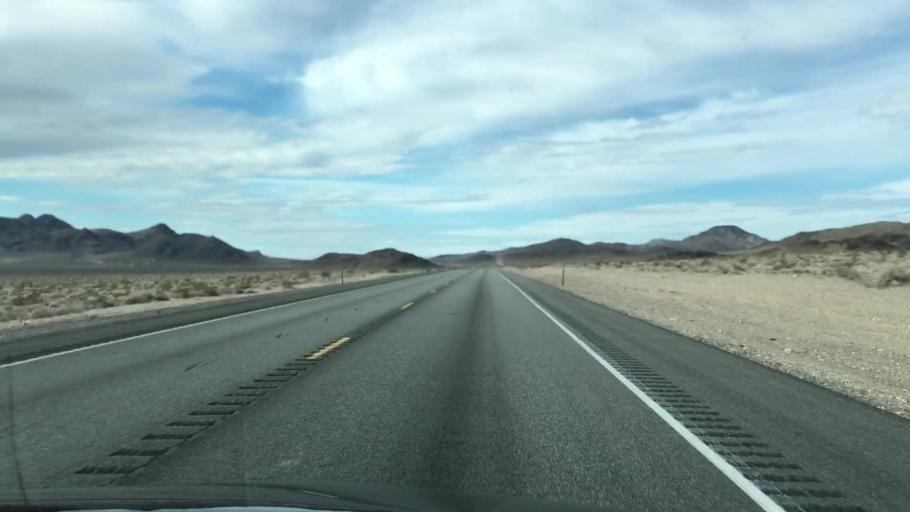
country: US
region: Nevada
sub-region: Nye County
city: Pahrump
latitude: 36.6167
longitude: -116.2849
